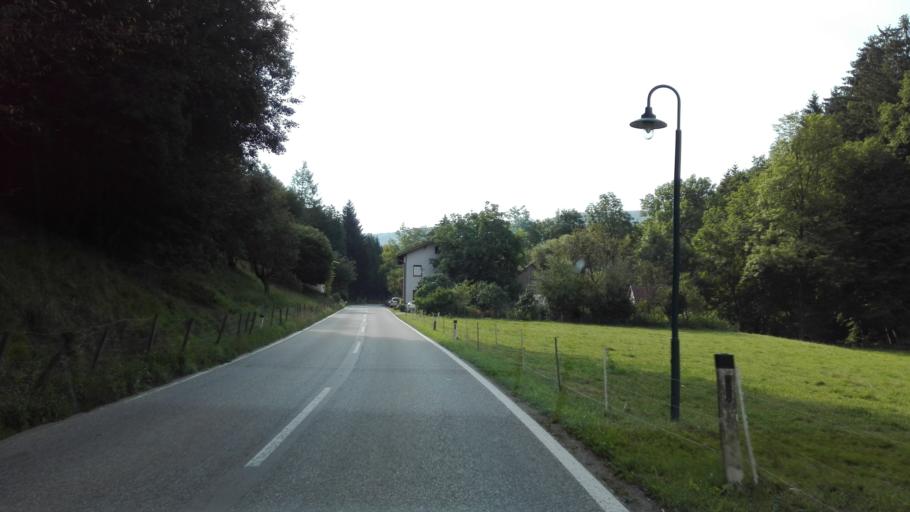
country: AT
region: Lower Austria
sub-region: Politischer Bezirk Sankt Polten
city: Stossing
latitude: 48.0952
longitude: 15.7704
